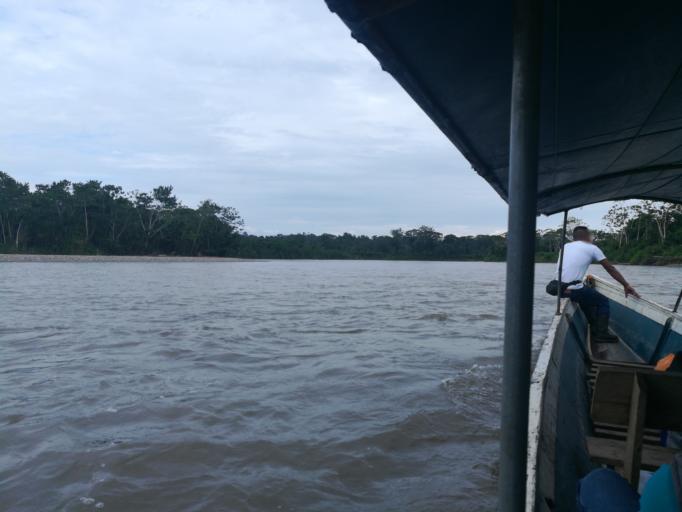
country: EC
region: Orellana
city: Boca Suno
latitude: -0.7589
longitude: -77.1535
